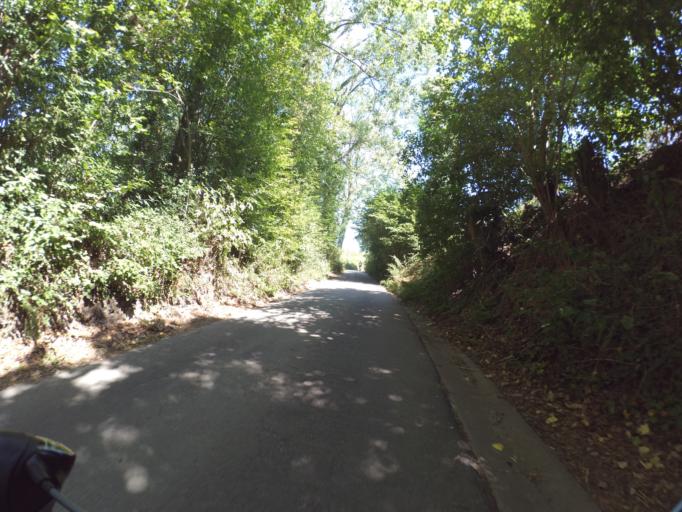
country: BE
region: Flanders
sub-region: Provincie Oost-Vlaanderen
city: Oudenaarde
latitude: 50.8225
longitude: 3.6272
